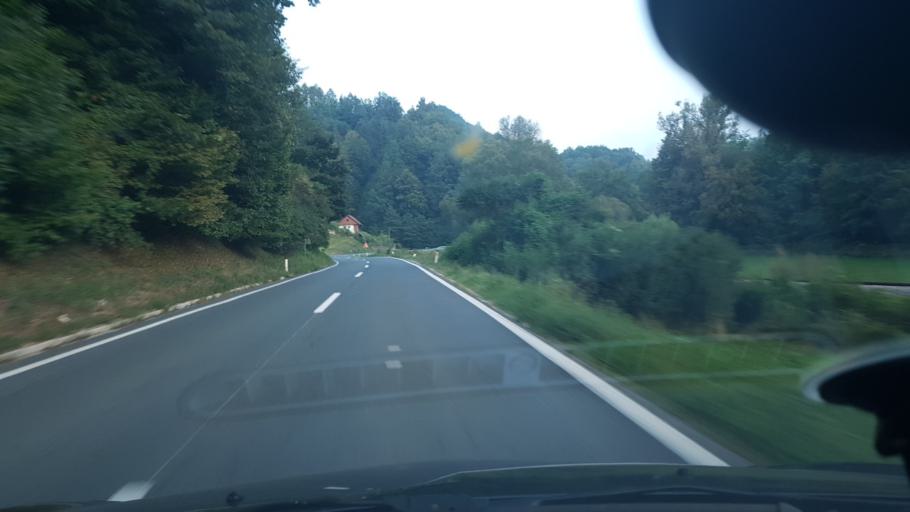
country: SI
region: Rogatec
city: Rogatec
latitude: 46.2206
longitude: 15.7534
